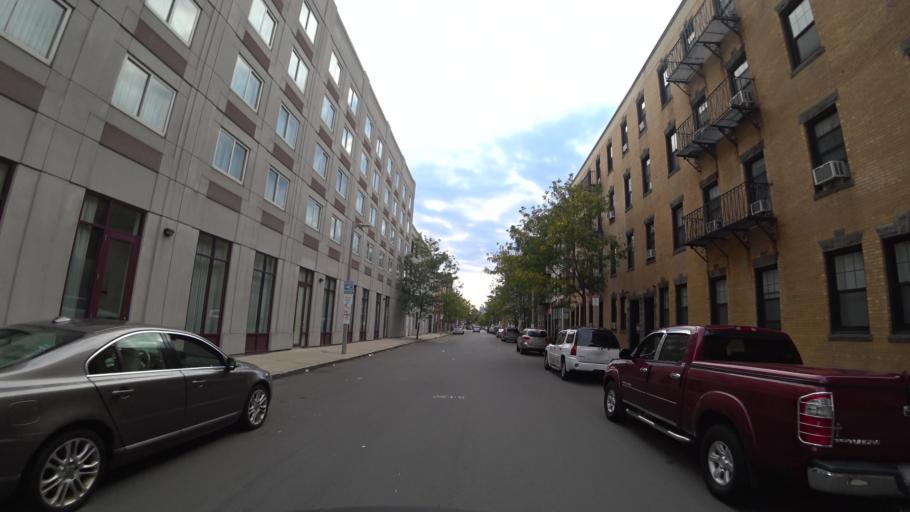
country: US
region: Massachusetts
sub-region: Suffolk County
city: Chelsea
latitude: 42.3706
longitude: -71.0320
